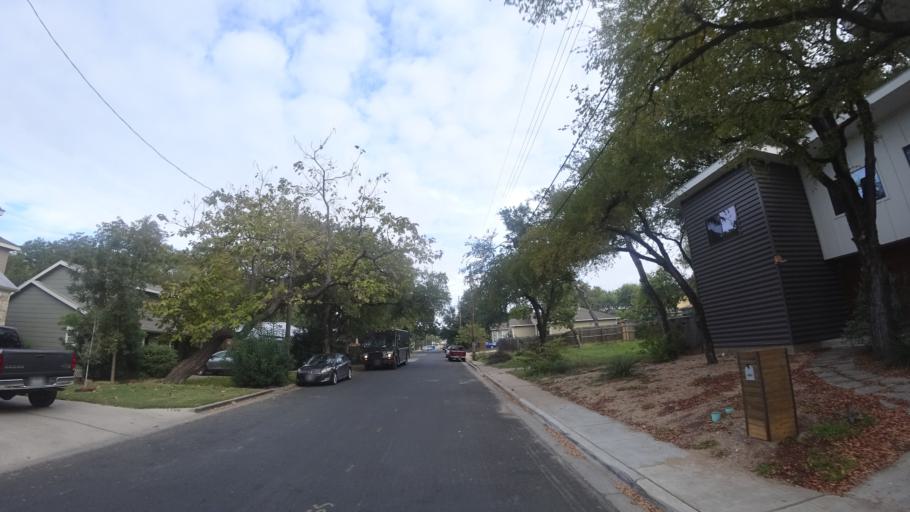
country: US
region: Texas
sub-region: Travis County
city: Austin
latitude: 30.2797
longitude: -97.7072
